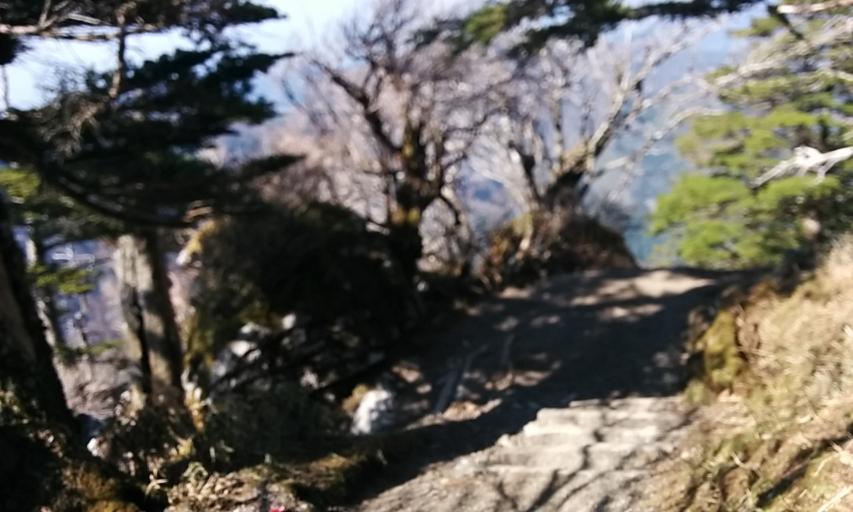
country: JP
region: Tokushima
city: Wakimachi
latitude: 33.8579
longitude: 134.0953
